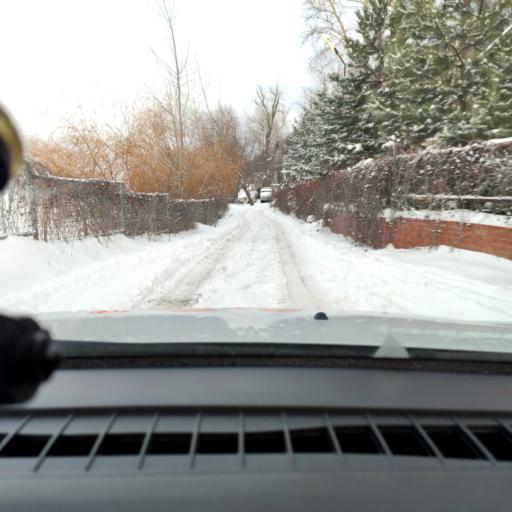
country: RU
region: Samara
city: Samara
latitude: 53.2837
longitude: 50.1896
